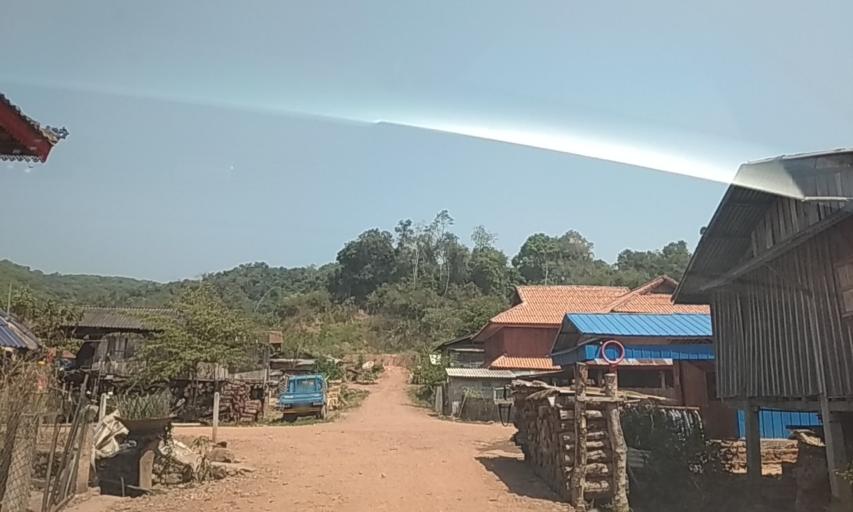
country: CN
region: Yunnan
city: Mengla
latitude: 21.5375
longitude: 101.8306
